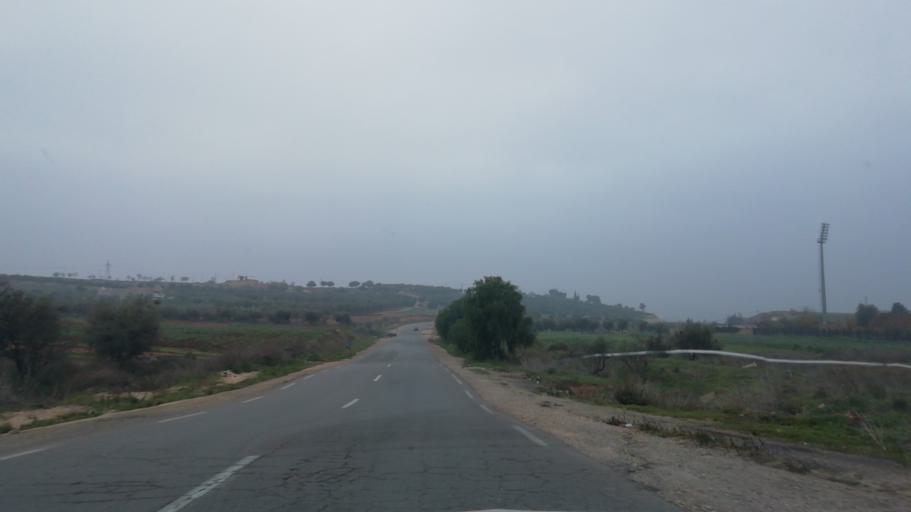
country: DZ
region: Mascara
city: Mascara
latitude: 35.3899
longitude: 0.1611
